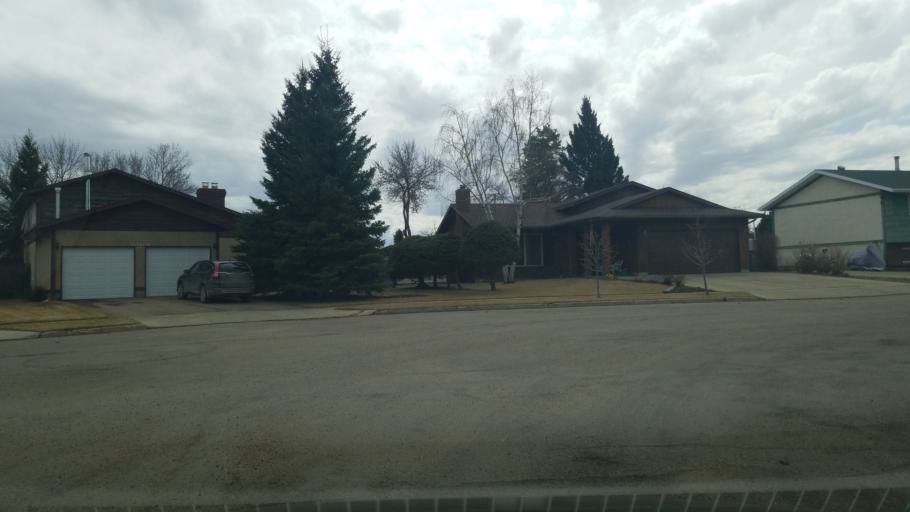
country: CA
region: Saskatchewan
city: Lloydminster
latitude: 53.2649
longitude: -110.0271
